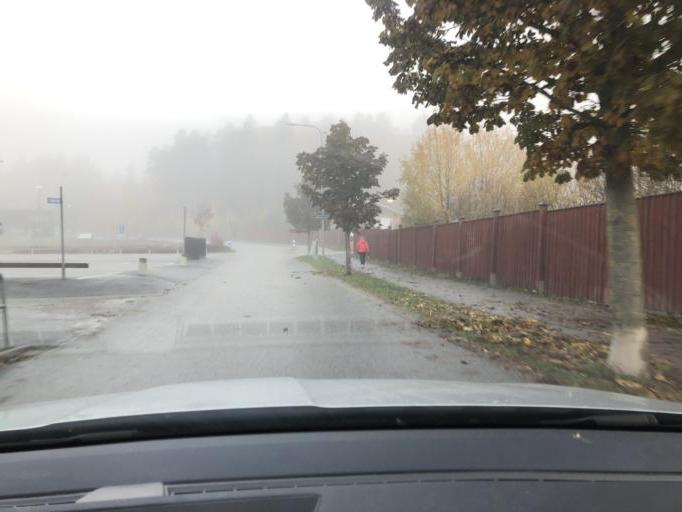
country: SE
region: Stockholm
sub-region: Huddinge Kommun
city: Segeltorp
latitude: 59.2672
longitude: 17.9312
